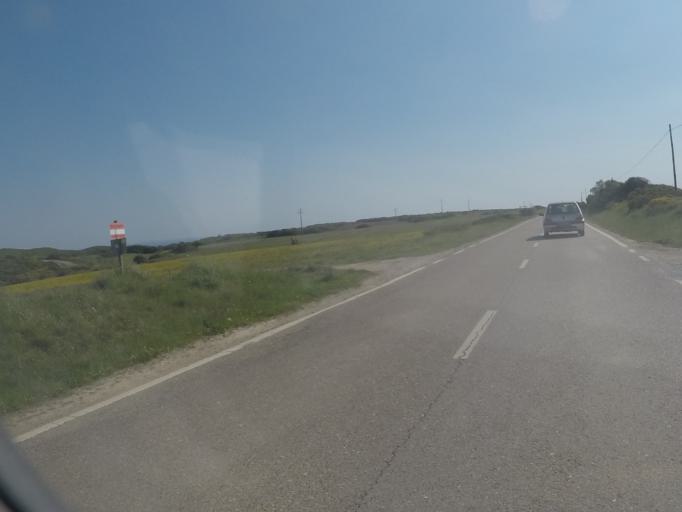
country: PT
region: Setubal
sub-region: Sesimbra
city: Sesimbra
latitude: 38.4241
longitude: -9.1962
